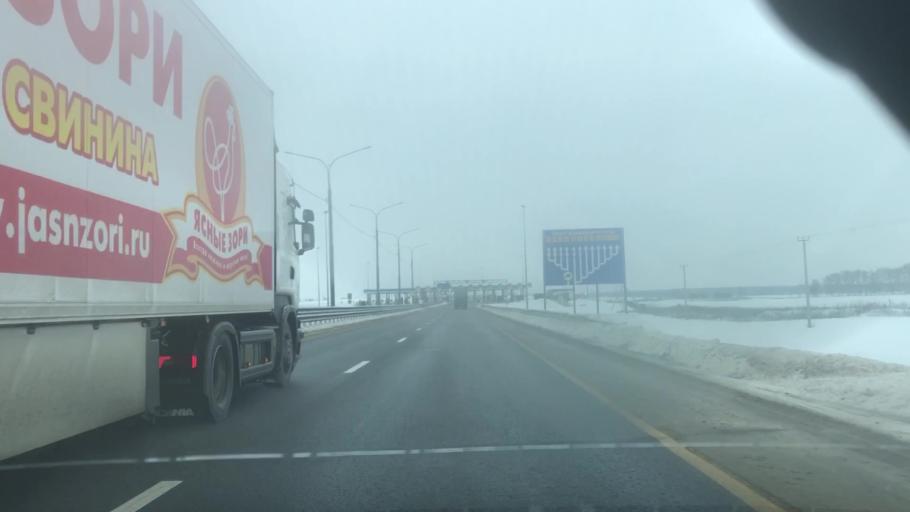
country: RU
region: Tula
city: Dubovka
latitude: 53.8821
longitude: 38.0504
